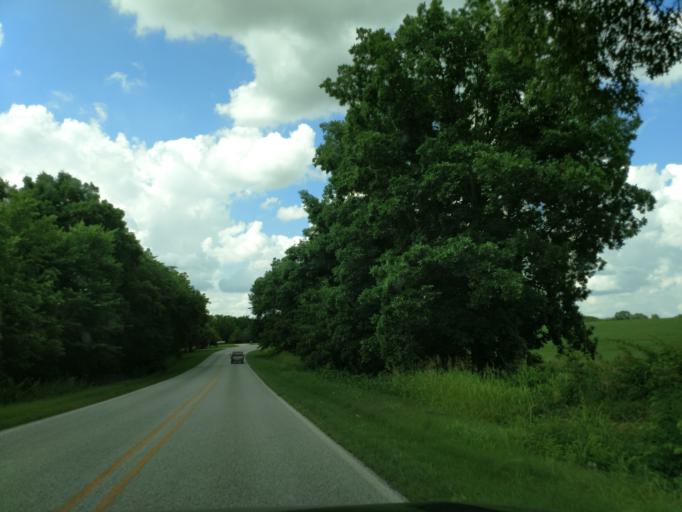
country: US
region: Arkansas
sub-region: Carroll County
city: Berryville
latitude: 36.4044
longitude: -93.5660
